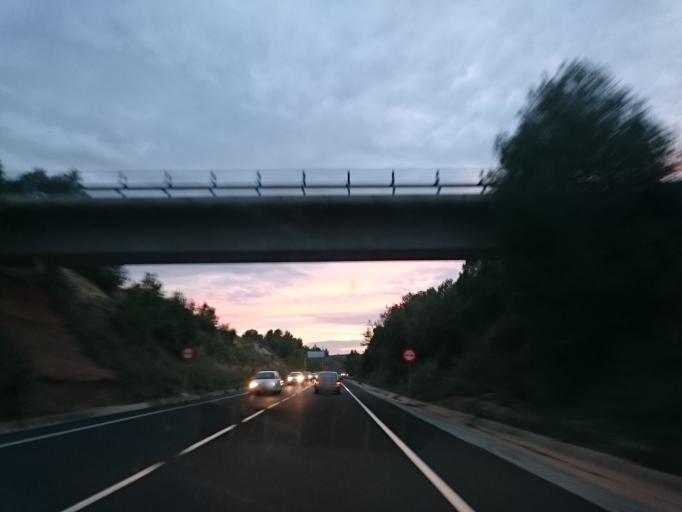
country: ES
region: Catalonia
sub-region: Provincia de Barcelona
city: Sant Pere de Riudebitlles
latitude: 41.4877
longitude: 1.7034
